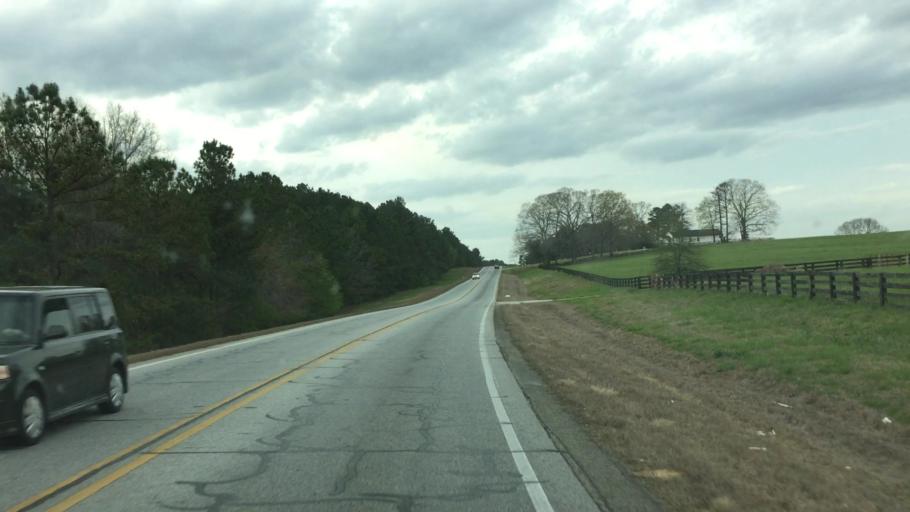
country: US
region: Georgia
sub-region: Jackson County
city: Hoschton
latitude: 34.0785
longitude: -83.7411
